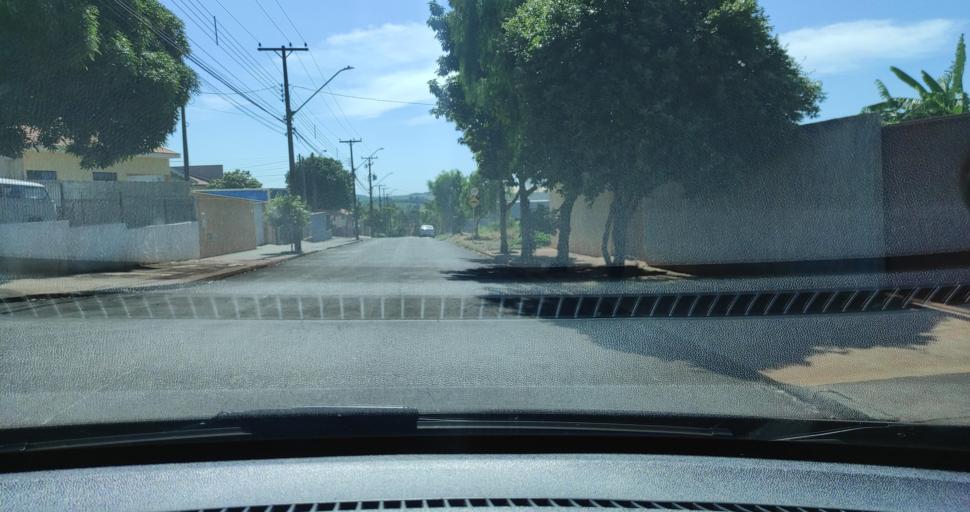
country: BR
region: Parana
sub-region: Ibipora
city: Ibipora
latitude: -23.2588
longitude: -51.0584
